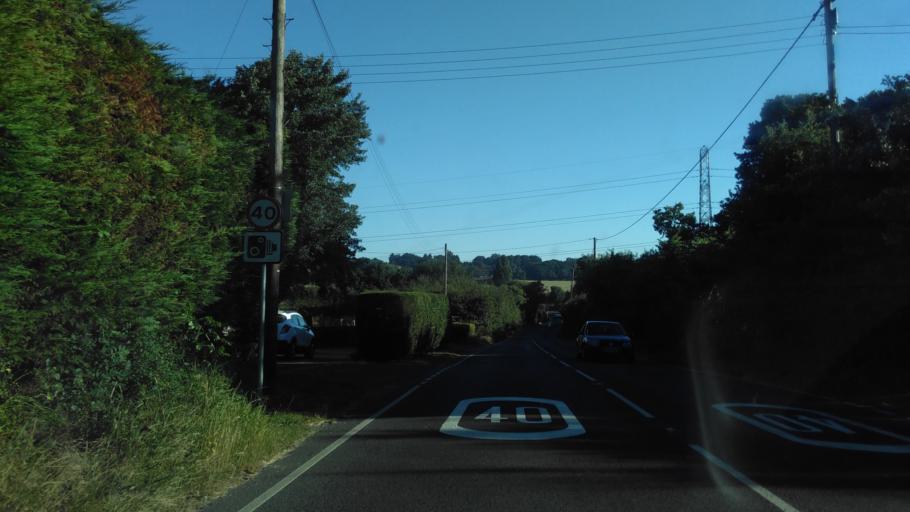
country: GB
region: England
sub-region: Kent
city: Blean
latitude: 51.3301
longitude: 1.0243
